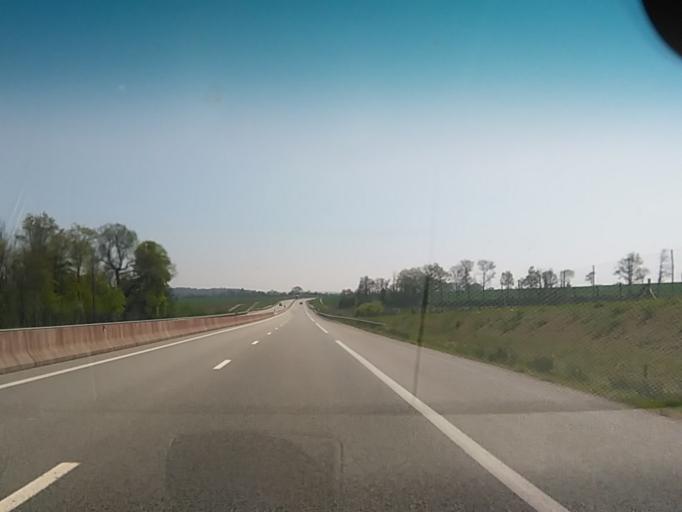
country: FR
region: Lower Normandy
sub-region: Departement de l'Orne
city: Mortree
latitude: 48.6815
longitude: 0.0361
